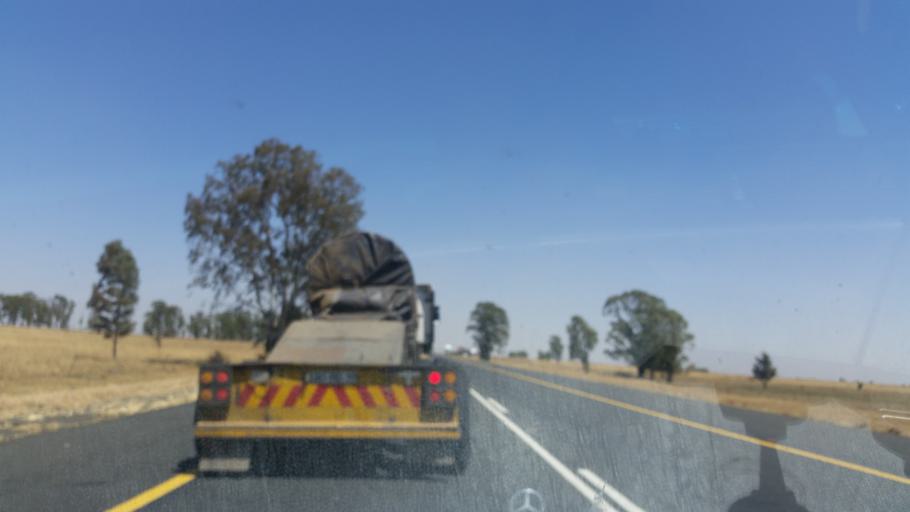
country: ZA
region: Orange Free State
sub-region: Lejweleputswa District Municipality
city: Winburg
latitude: -28.6400
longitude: 26.8912
